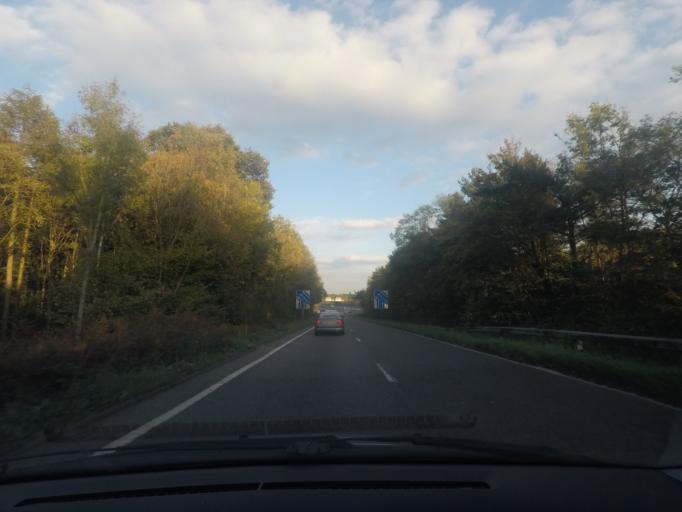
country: GB
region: England
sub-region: North Lincolnshire
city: Scawby
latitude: 53.5447
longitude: -0.5556
